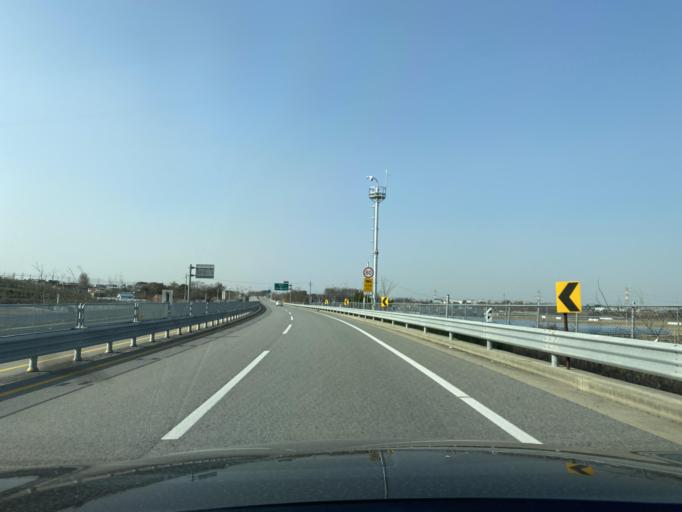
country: KR
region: Chungcheongnam-do
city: Yesan
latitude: 36.7576
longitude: 126.8290
